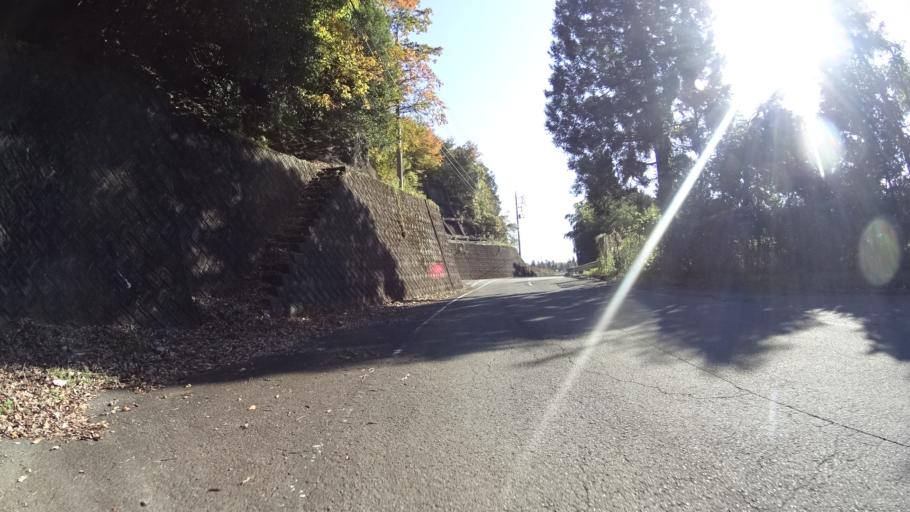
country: JP
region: Yamanashi
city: Uenohara
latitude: 35.6695
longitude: 139.1013
